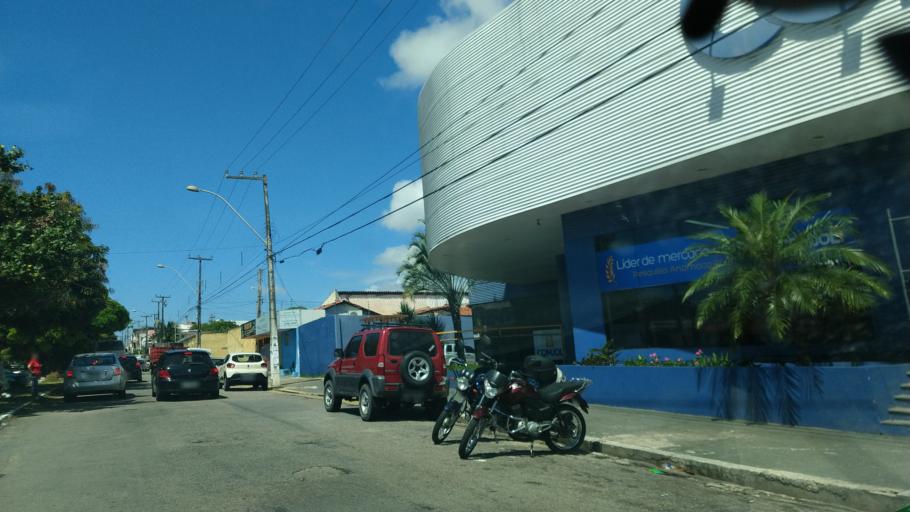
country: BR
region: Rio Grande do Norte
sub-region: Natal
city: Natal
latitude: -5.8039
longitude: -35.2143
